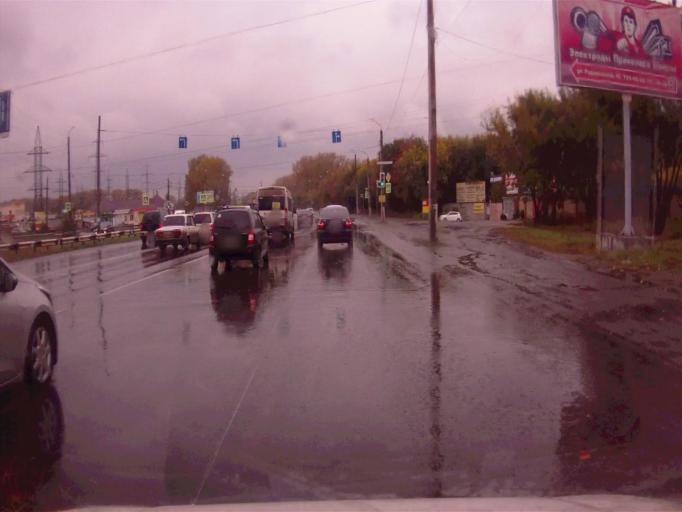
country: RU
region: Chelyabinsk
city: Dolgoderevenskoye
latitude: 55.2405
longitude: 61.3612
